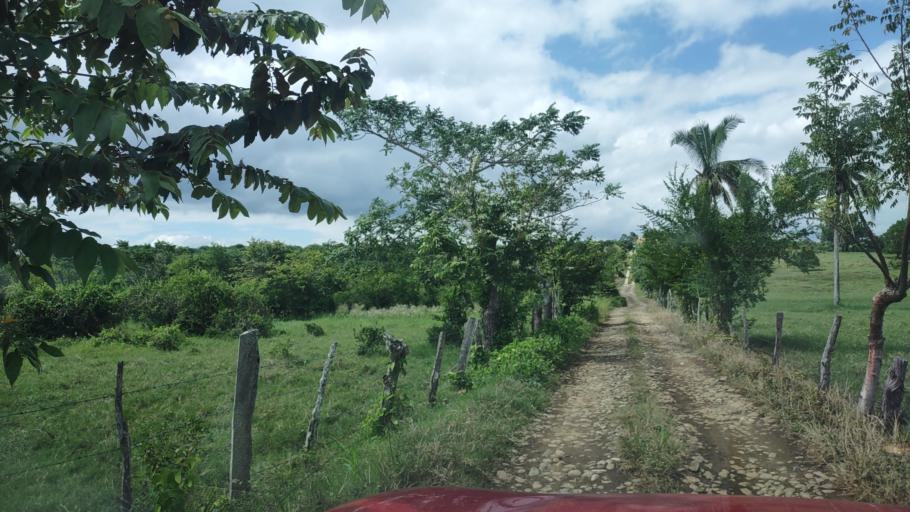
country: MX
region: Puebla
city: San Jose Acateno
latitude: 20.2189
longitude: -97.1389
